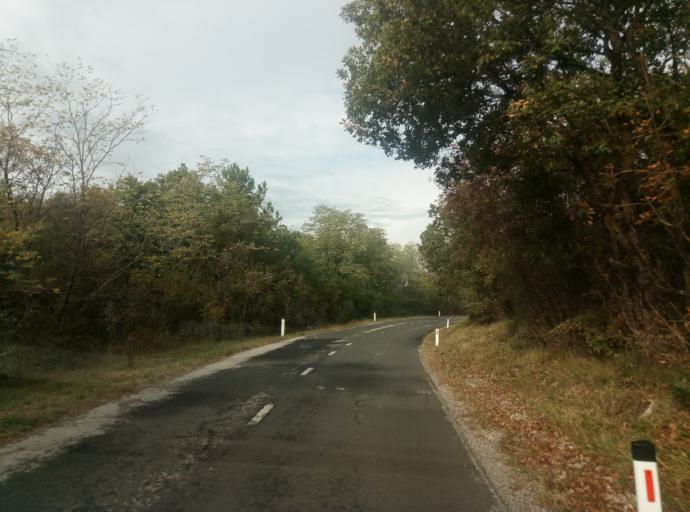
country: SI
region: Sezana
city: Sezana
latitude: 45.7777
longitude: 13.8681
